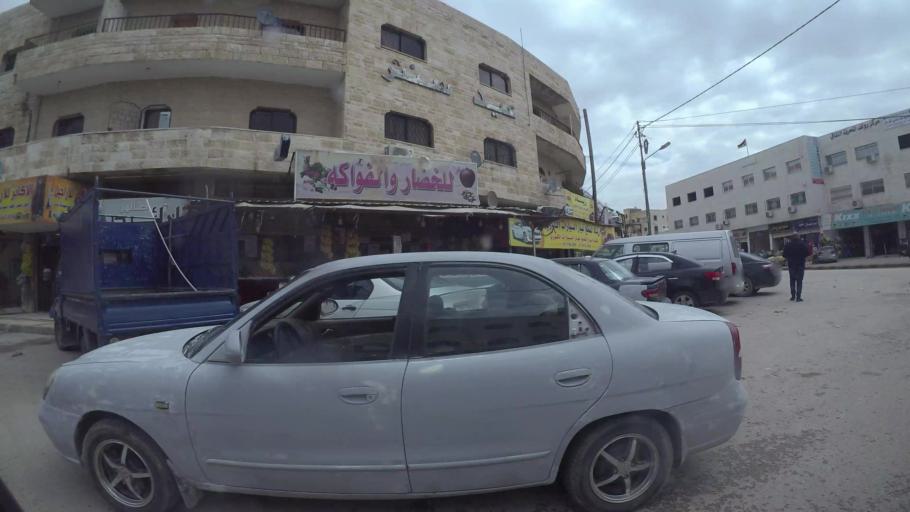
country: JO
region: Amman
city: Al Jubayhah
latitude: 32.0548
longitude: 35.8343
